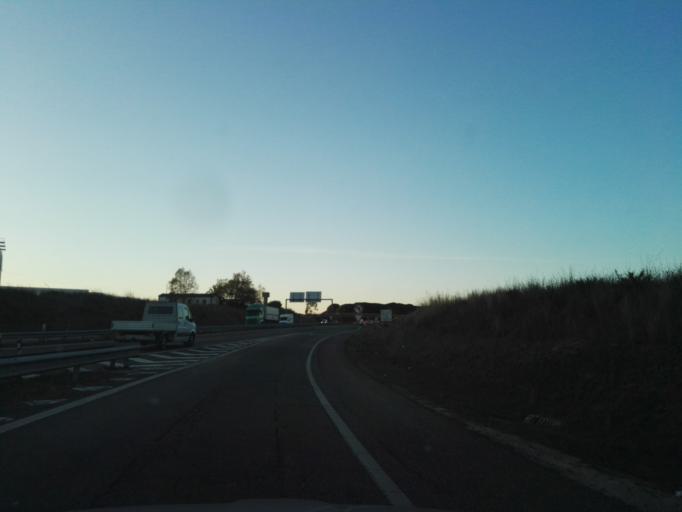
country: PT
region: Santarem
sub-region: Santarem
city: Santarem
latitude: 39.2606
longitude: -8.7050
